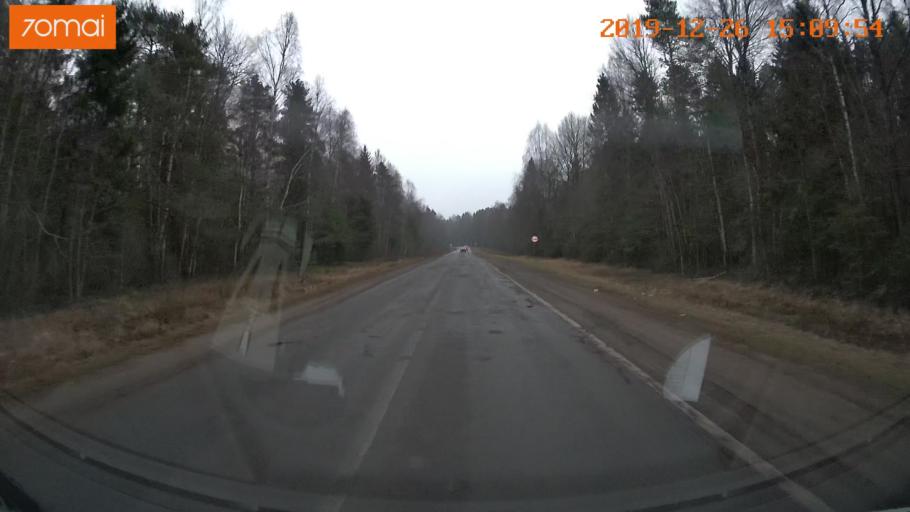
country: RU
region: Jaroslavl
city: Rybinsk
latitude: 58.1450
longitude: 38.8454
